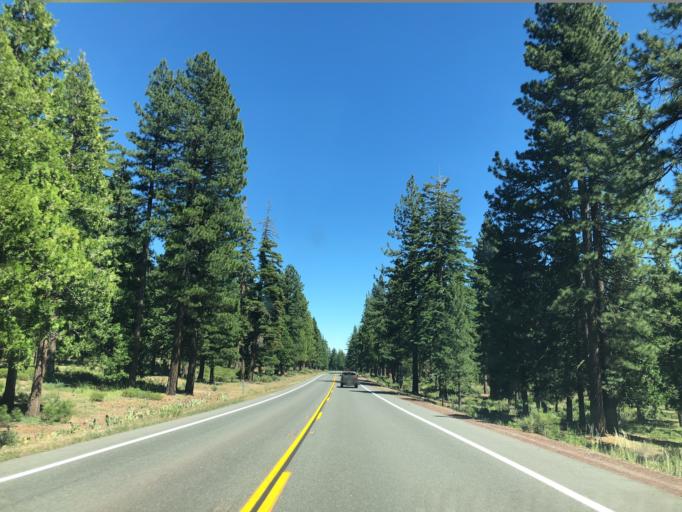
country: US
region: California
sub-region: Lassen County
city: Susanville
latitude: 40.4283
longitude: -120.8185
